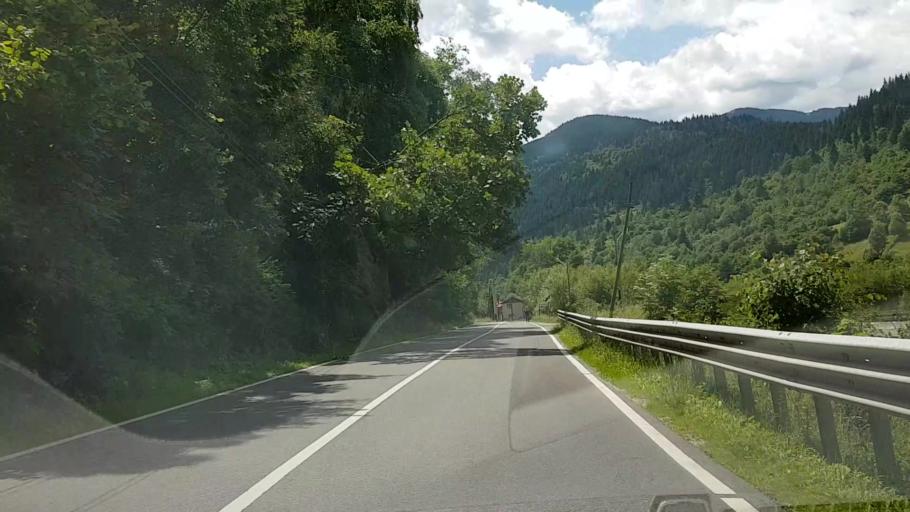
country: RO
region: Suceava
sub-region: Comuna Brosteni
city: Brosteni
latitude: 47.2522
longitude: 25.6962
